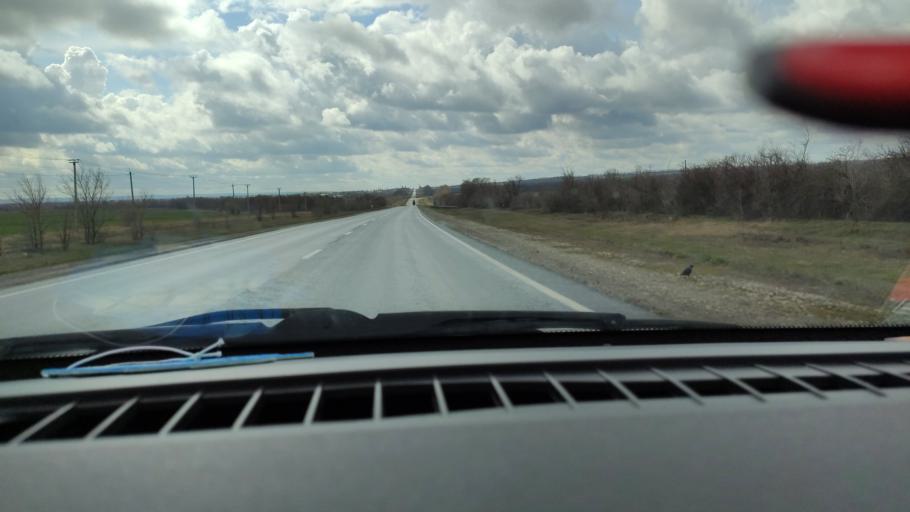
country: RU
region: Samara
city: Yelkhovka
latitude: 53.8991
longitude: 50.2687
